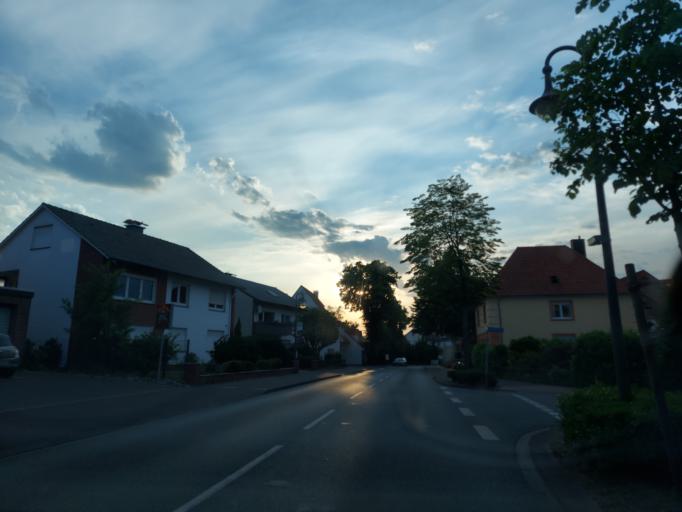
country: DE
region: North Rhine-Westphalia
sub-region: Regierungsbezirk Detmold
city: Verl
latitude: 51.9358
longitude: 8.4839
